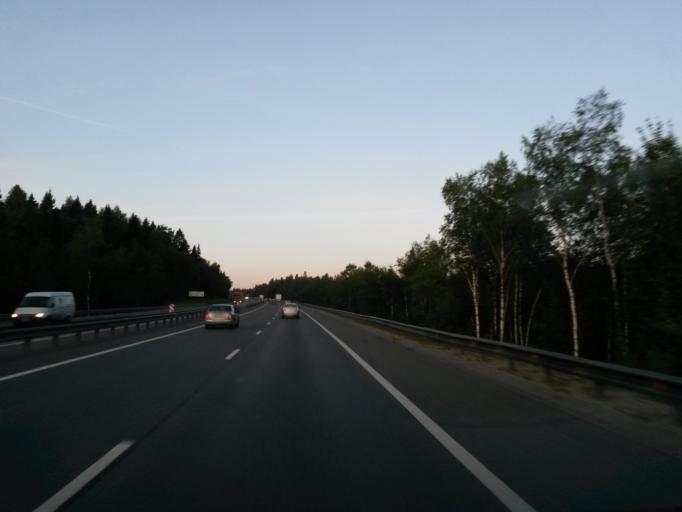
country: RU
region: Moskovskaya
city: Sergiyev Posad
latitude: 56.2656
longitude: 38.1830
